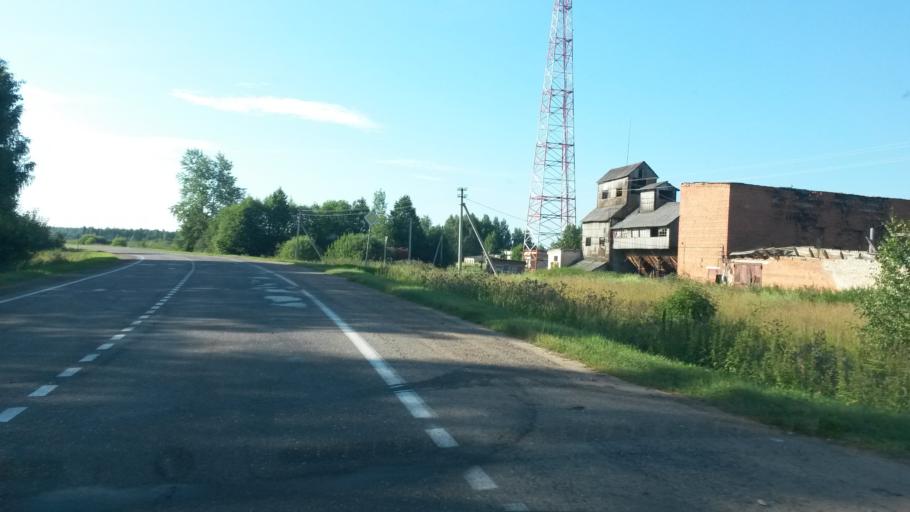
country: RU
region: Jaroslavl
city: Gavrilov-Yam
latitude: 57.3079
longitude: 39.9377
